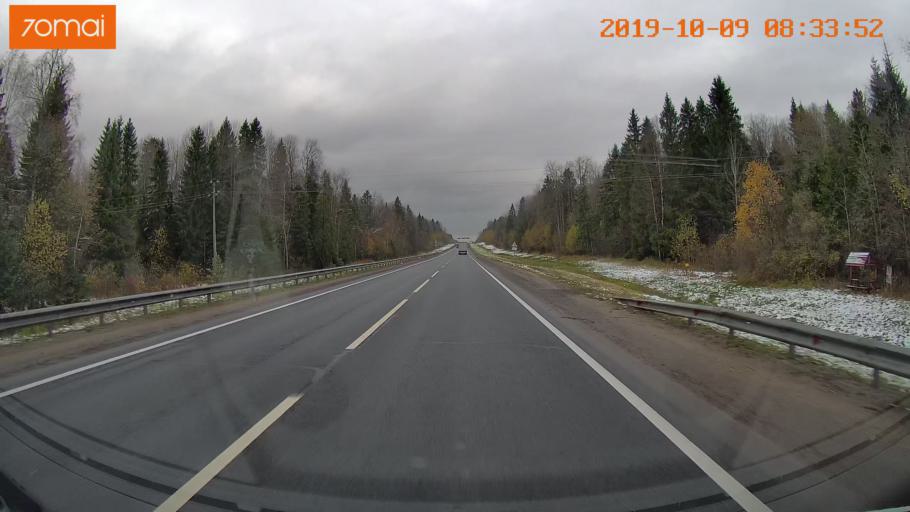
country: RU
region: Vologda
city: Gryazovets
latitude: 58.8886
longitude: 40.1894
